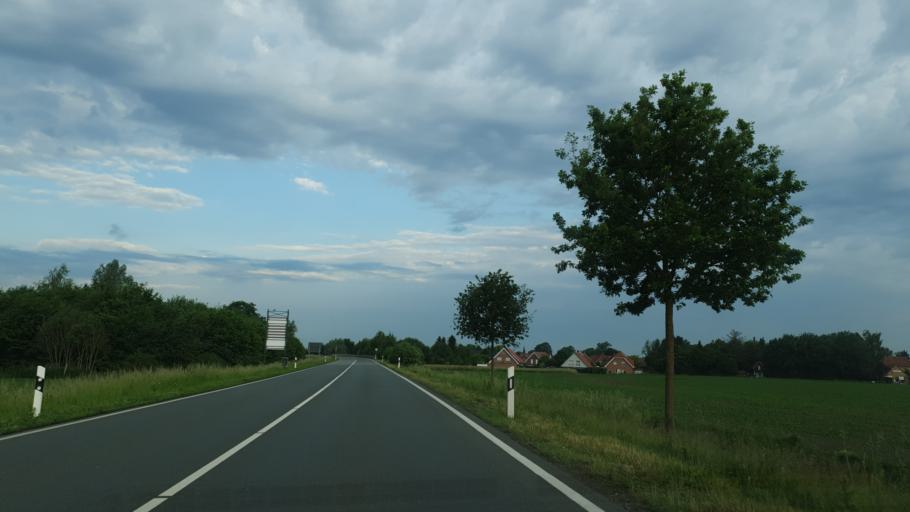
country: DE
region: North Rhine-Westphalia
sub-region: Regierungsbezirk Munster
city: Telgte
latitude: 52.0267
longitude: 7.7580
